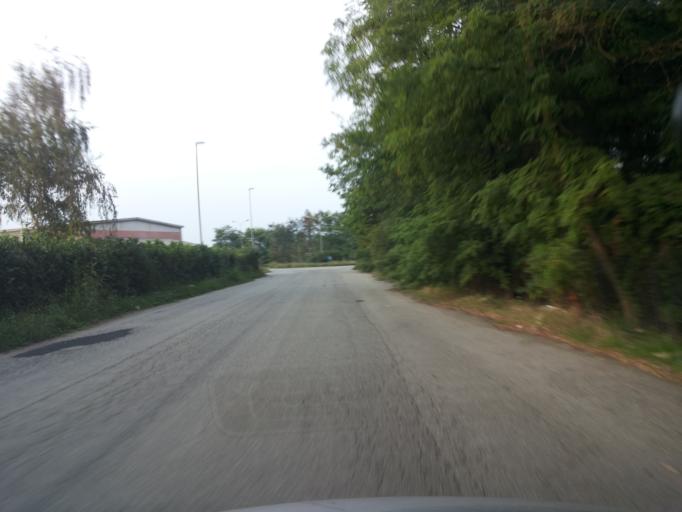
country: IT
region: Piedmont
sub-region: Provincia di Biella
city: Cavaglia
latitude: 45.3913
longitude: 8.1239
